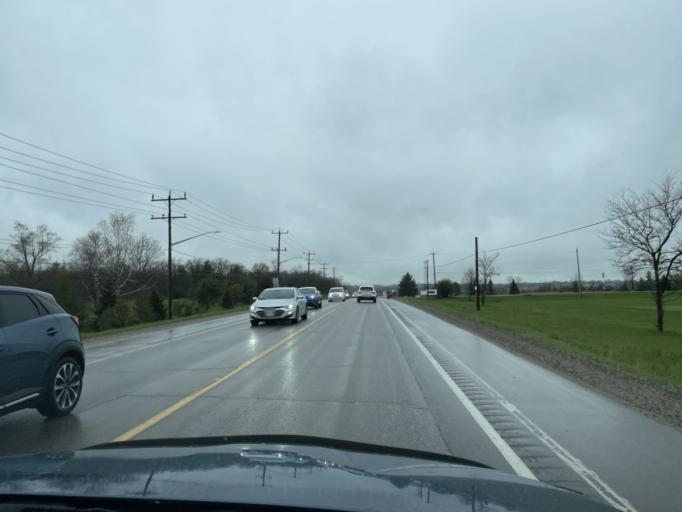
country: CA
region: Ontario
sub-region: Wellington County
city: Guelph
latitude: 43.5464
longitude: -80.2162
